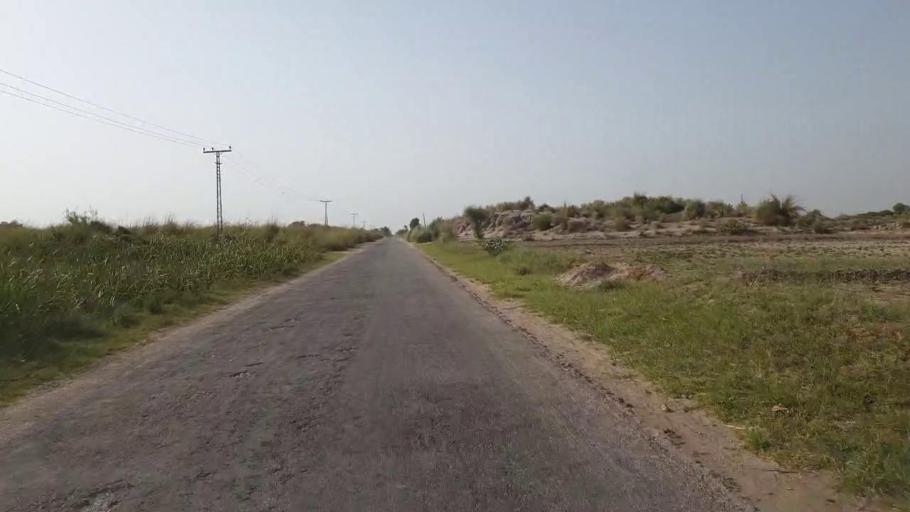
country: PK
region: Sindh
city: Khadro
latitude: 26.3543
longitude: 68.9216
